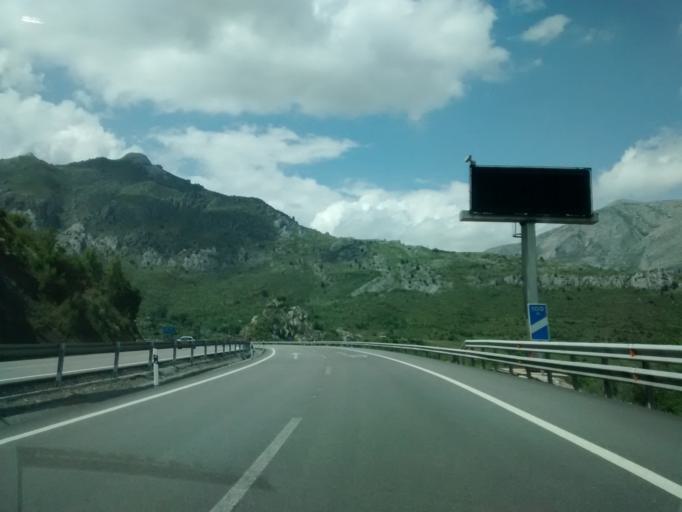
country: ES
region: Castille and Leon
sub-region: Provincia de Leon
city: Sena de Luna
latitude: 42.9057
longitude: -5.8891
